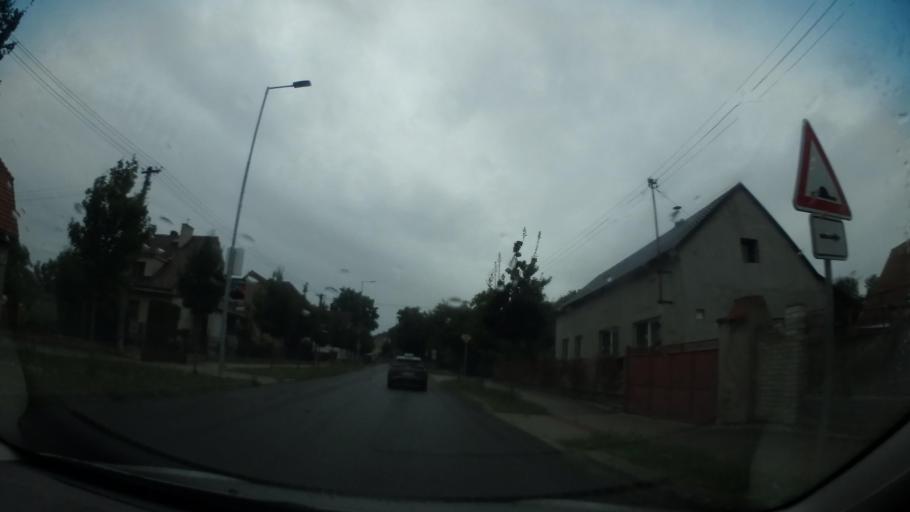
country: CZ
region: Central Bohemia
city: Milovice
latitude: 50.2264
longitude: 14.8823
